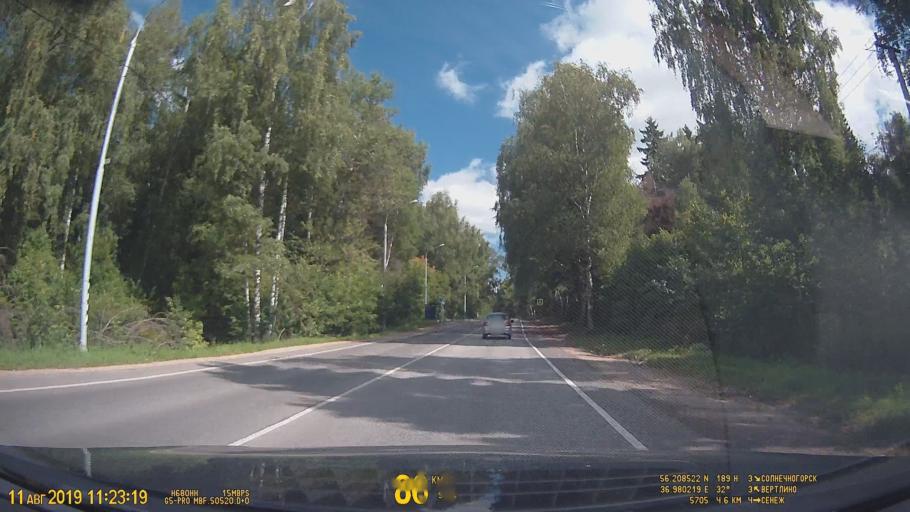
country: RU
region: Moskovskaya
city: Solnechnogorsk
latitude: 56.2088
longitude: 36.9806
